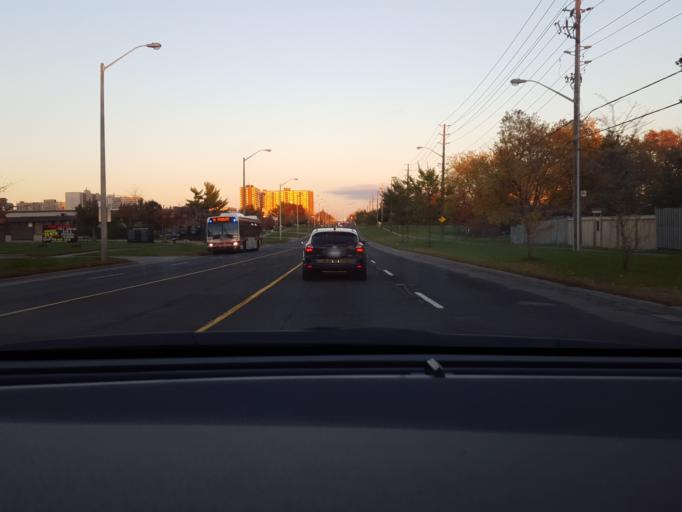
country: CA
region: Ontario
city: Scarborough
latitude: 43.7745
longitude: -79.2408
